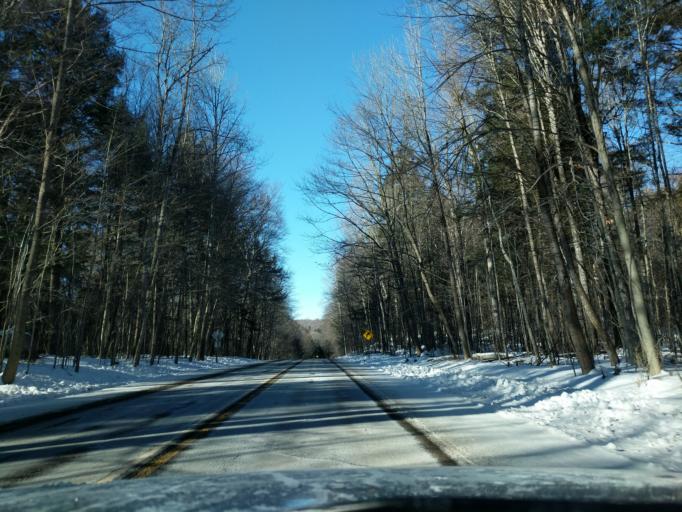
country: US
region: Wisconsin
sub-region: Menominee County
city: Keshena
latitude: 45.0912
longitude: -88.6302
